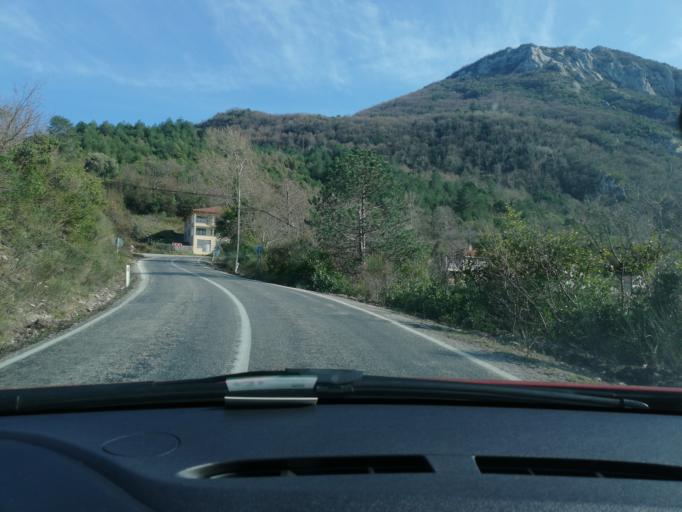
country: TR
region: Bartin
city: Kurucasile
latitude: 41.8463
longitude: 32.7579
